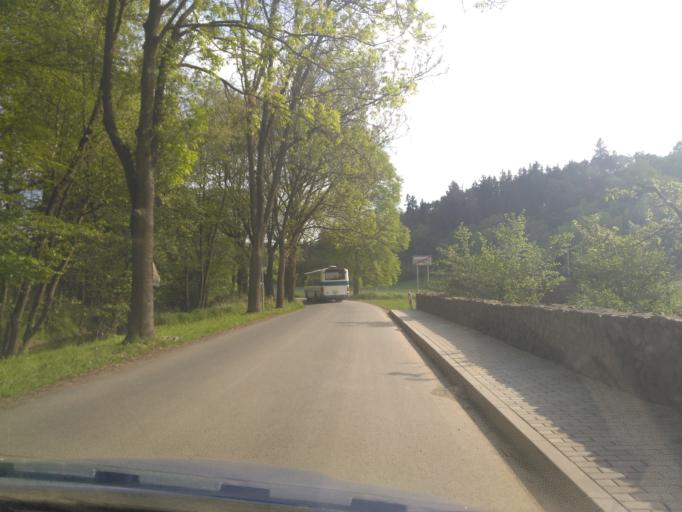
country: CZ
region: Central Bohemia
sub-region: Okres Beroun
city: Lodenice
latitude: 50.0178
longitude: 14.1417
